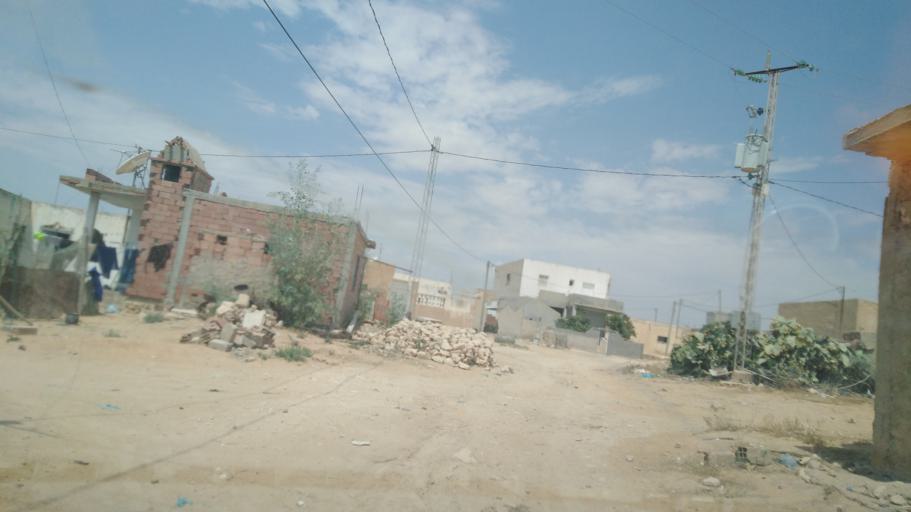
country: TN
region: Safaqis
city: Sfax
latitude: 34.7412
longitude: 10.5616
